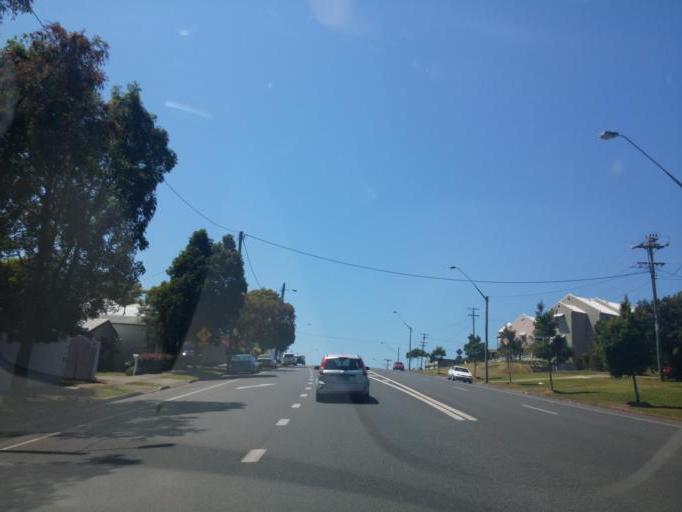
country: AU
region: New South Wales
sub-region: Coffs Harbour
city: Coffs Harbour
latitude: -30.3052
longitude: 153.1333
